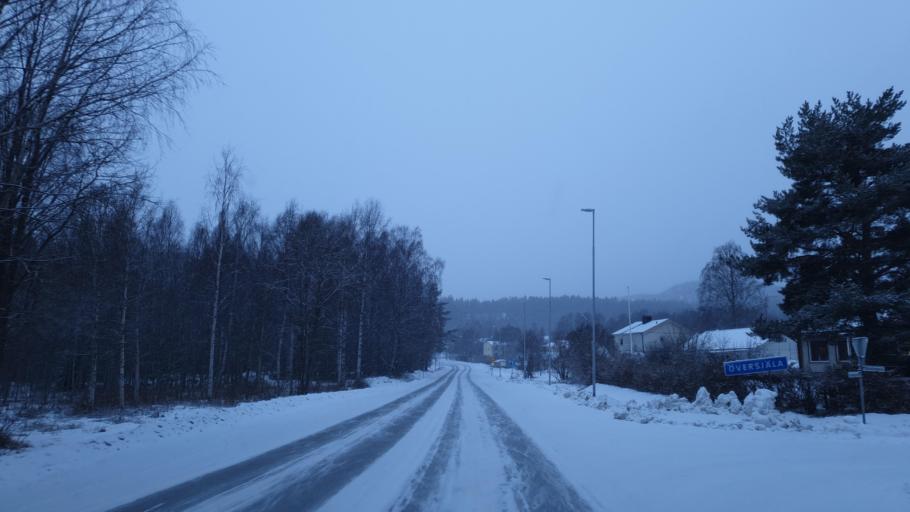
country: SE
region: Vaesternorrland
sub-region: OErnskoeldsviks Kommun
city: Ornskoldsvik
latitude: 63.3000
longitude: 18.6416
